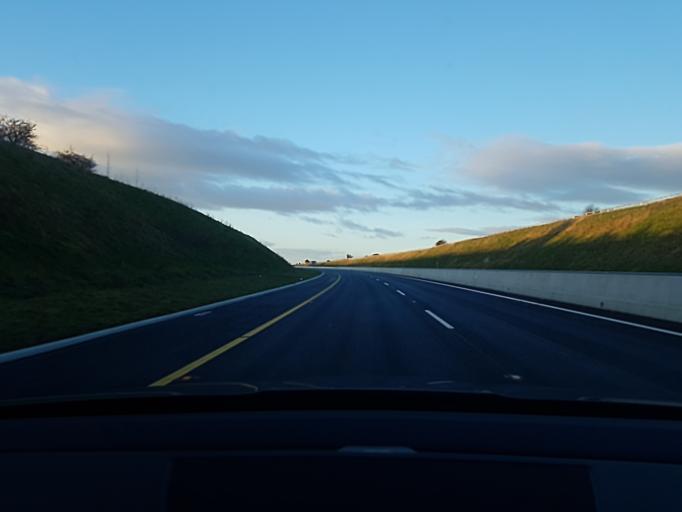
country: IE
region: Connaught
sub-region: County Galway
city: Athenry
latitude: 53.3651
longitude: -8.7878
